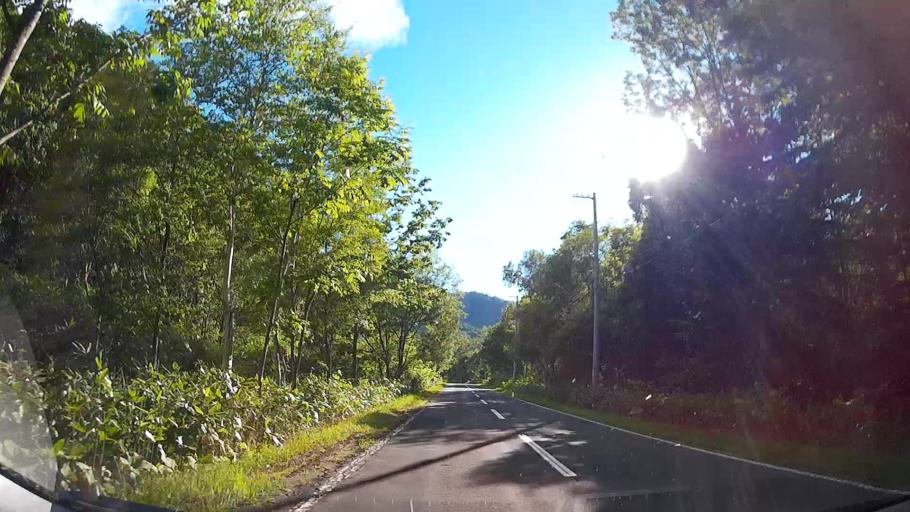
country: JP
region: Hokkaido
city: Sapporo
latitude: 42.9726
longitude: 141.1535
